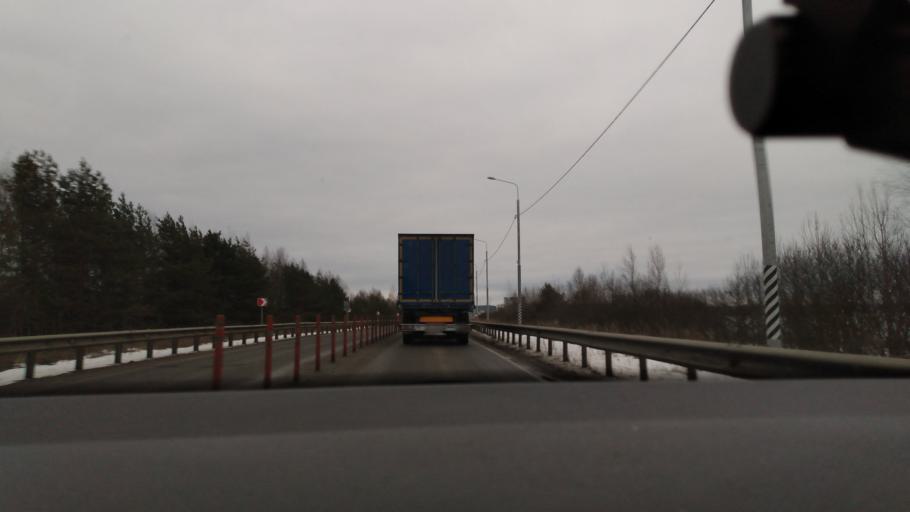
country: RU
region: Moskovskaya
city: Yegor'yevsk
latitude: 55.4460
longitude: 39.0131
